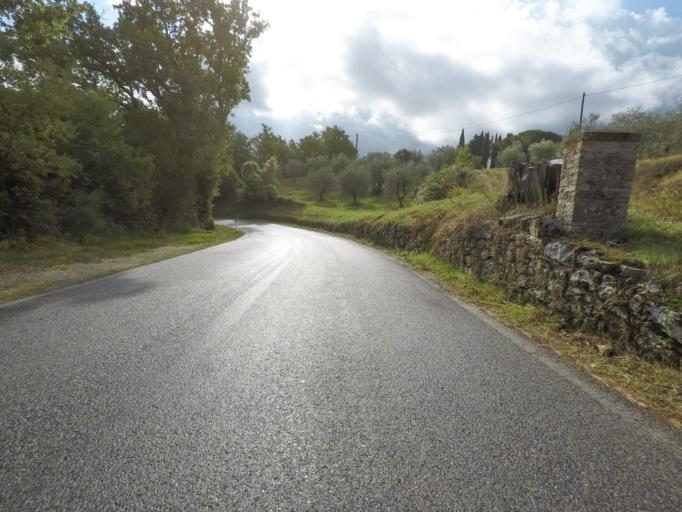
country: IT
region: Tuscany
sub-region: Provincia di Siena
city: Radda in Chianti
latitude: 43.4149
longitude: 11.3490
